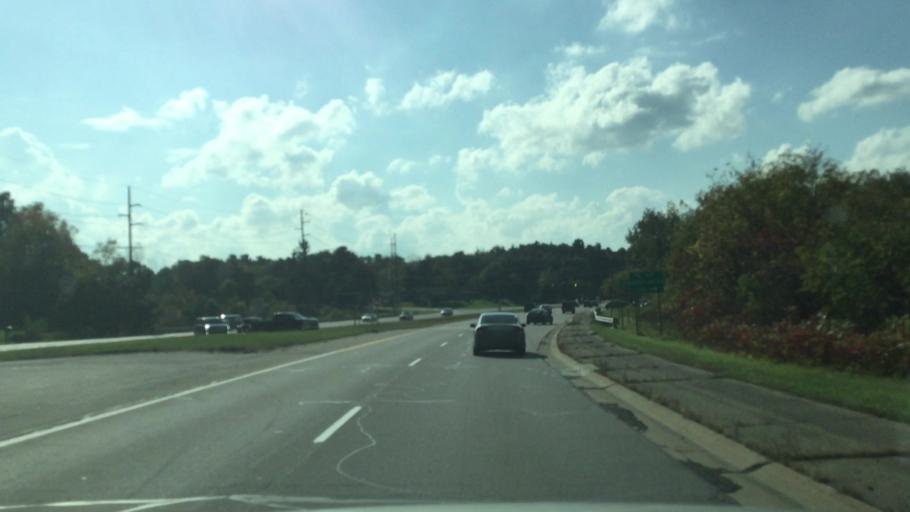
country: US
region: Michigan
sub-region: Oakland County
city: Milford
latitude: 42.6432
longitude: -83.6023
